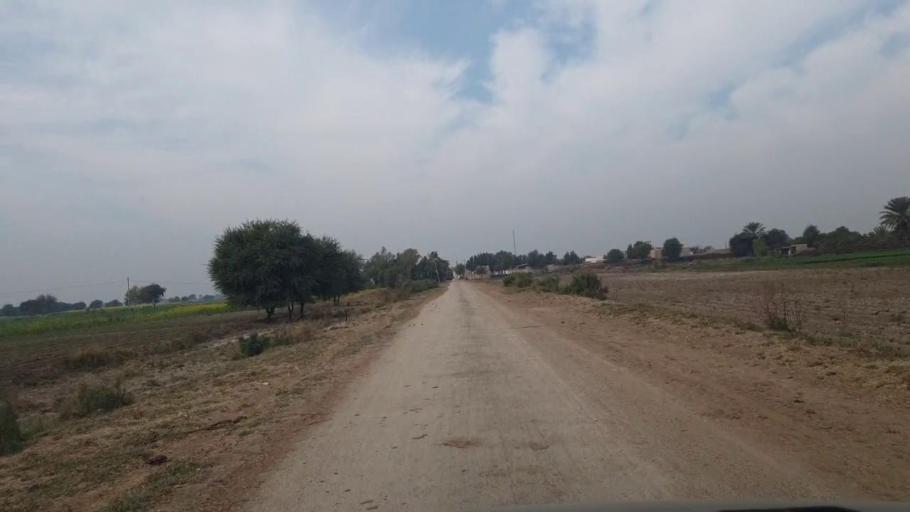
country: PK
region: Sindh
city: Shahdadpur
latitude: 25.9405
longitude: 68.6760
